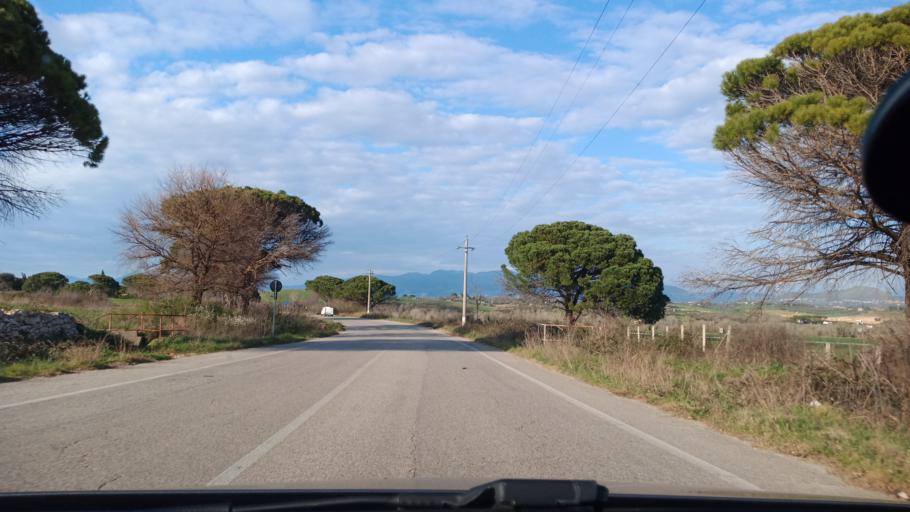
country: IT
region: Latium
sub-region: Citta metropolitana di Roma Capitale
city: Fiano Romano
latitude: 42.1629
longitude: 12.6210
